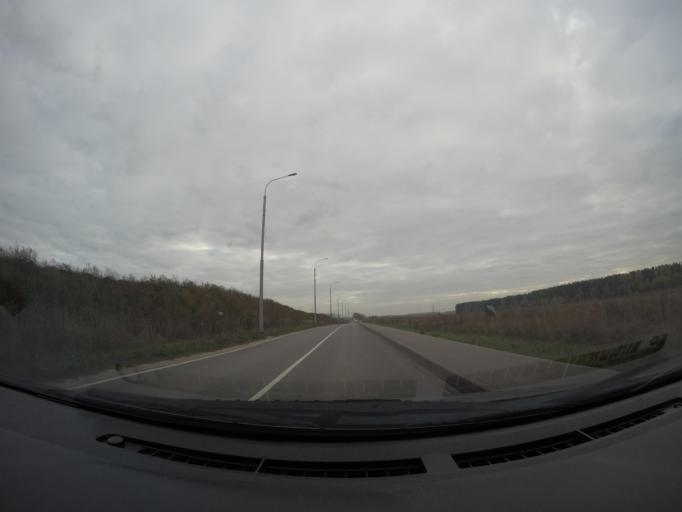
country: RU
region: Moskovskaya
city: Vishnyakovskiye Dachi
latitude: 55.8054
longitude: 38.1340
